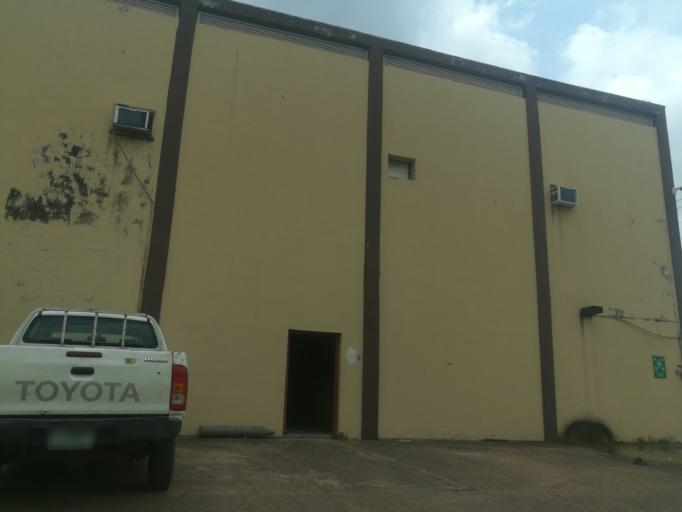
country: NG
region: Oyo
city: Ibadan
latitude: 7.3729
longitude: 3.8558
